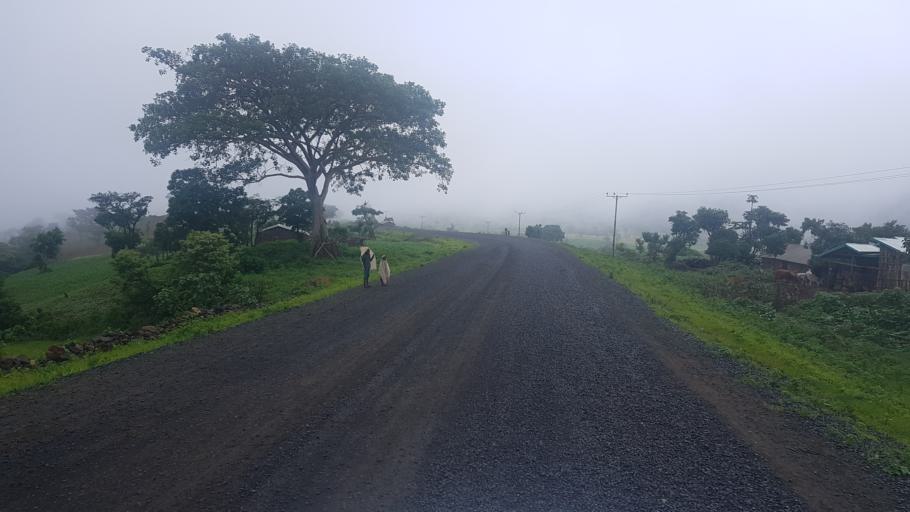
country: ET
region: Amhara
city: Bure
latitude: 10.1953
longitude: 36.9743
